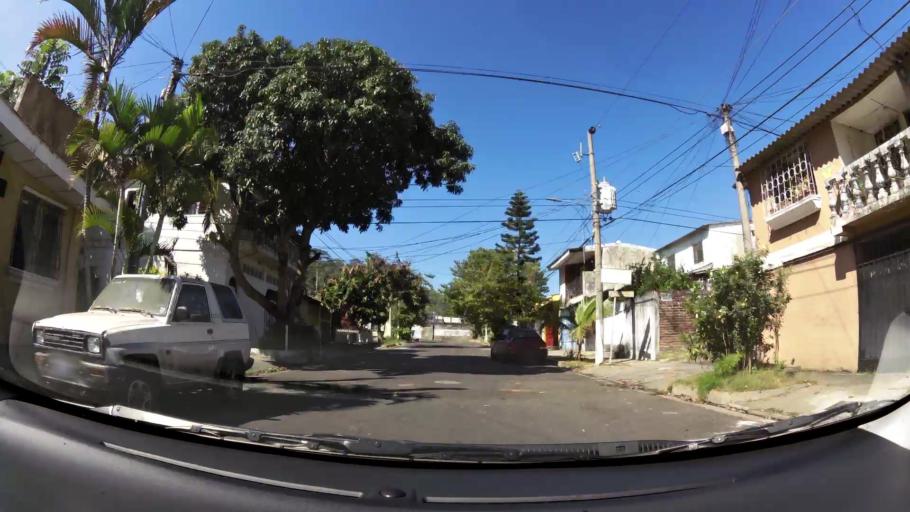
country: SV
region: La Libertad
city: Santa Tecla
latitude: 13.6677
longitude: -89.2876
